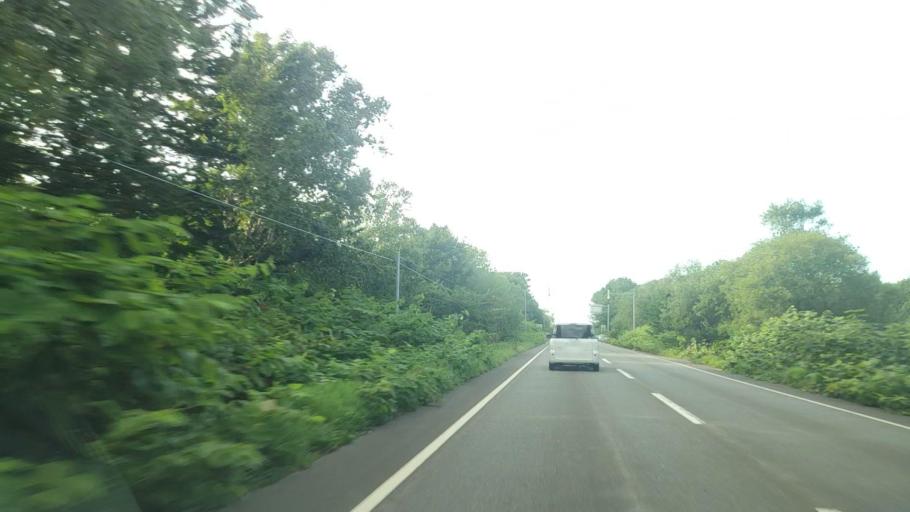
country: JP
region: Hokkaido
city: Makubetsu
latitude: 45.0515
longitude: 141.7506
